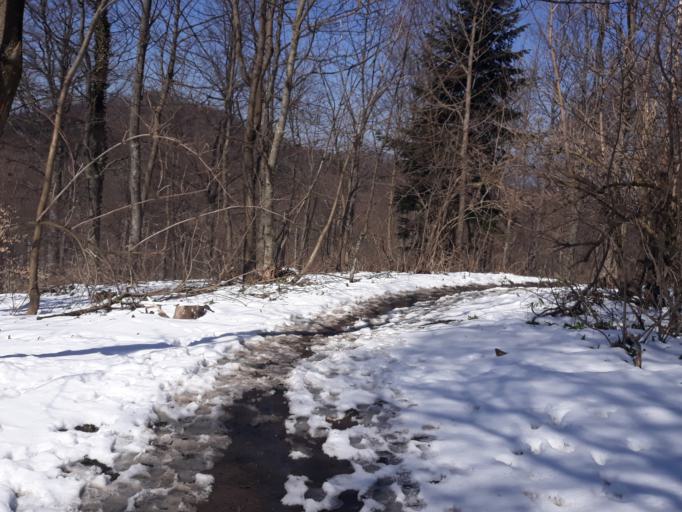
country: HR
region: Varazdinska
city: Ivanec
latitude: 46.1807
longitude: 16.1132
